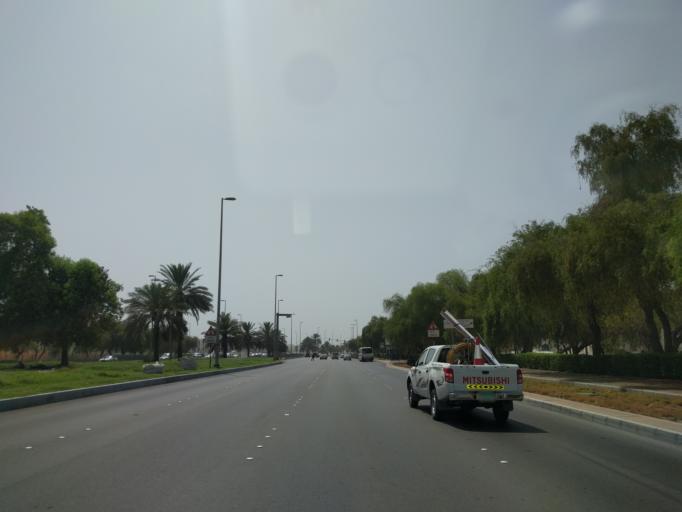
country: AE
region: Abu Dhabi
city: Abu Dhabi
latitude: 24.4407
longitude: 54.4094
